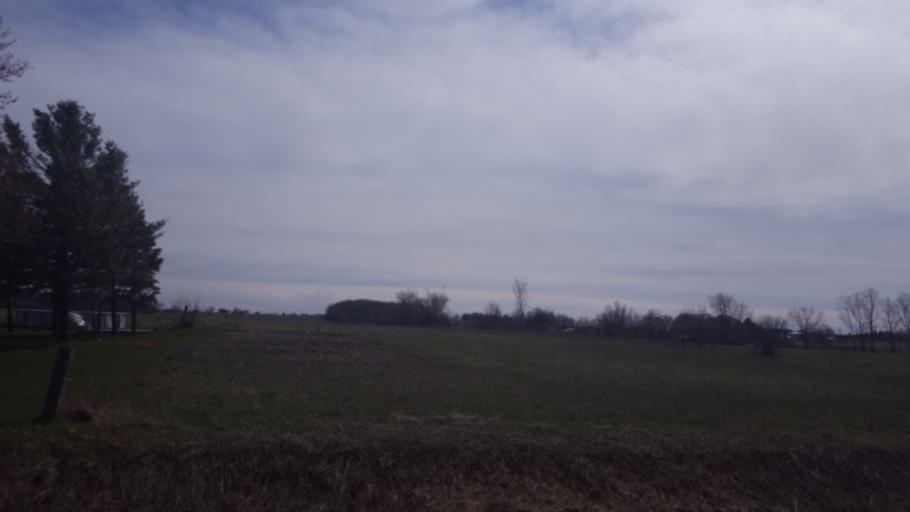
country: US
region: Michigan
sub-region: Gladwin County
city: Gladwin
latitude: 44.0308
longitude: -84.4815
